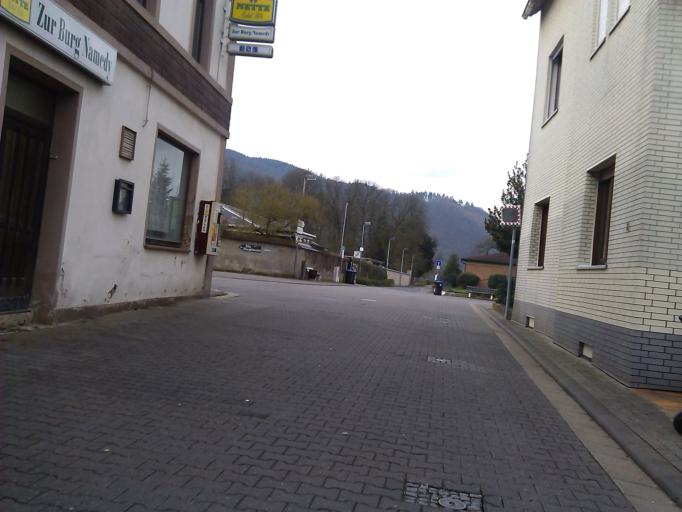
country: DE
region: Rheinland-Pfalz
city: Leutesdorf
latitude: 50.4555
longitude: 7.3594
